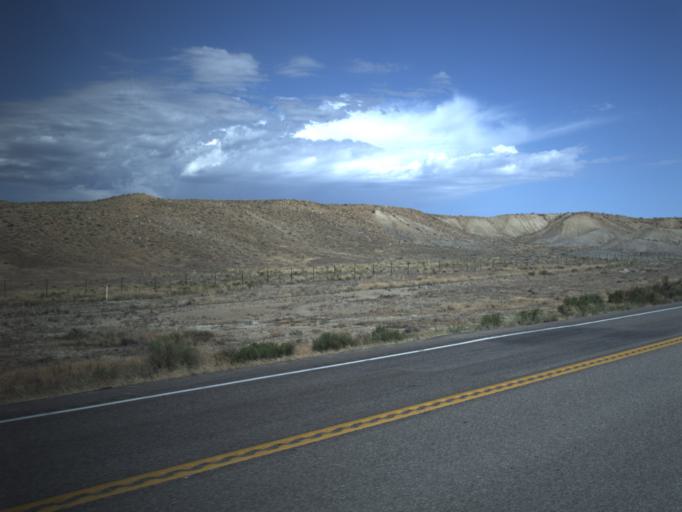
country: US
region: Utah
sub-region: Carbon County
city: East Carbon City
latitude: 39.2731
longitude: -110.3464
